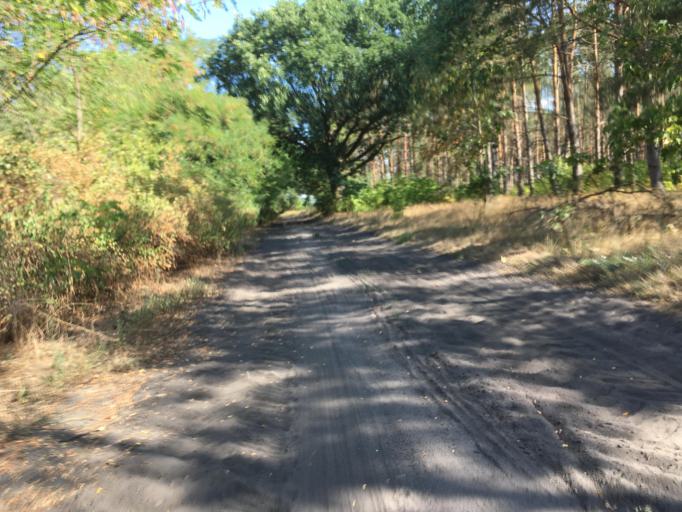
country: DE
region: Brandenburg
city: Zehdenick
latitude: 52.9660
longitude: 13.3838
